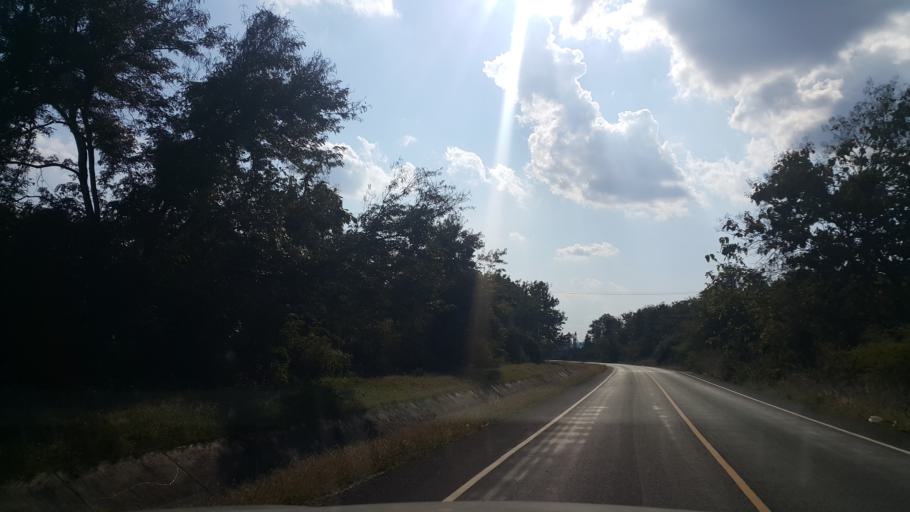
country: TH
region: Lamphun
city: Ban Thi
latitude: 18.5448
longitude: 99.1016
